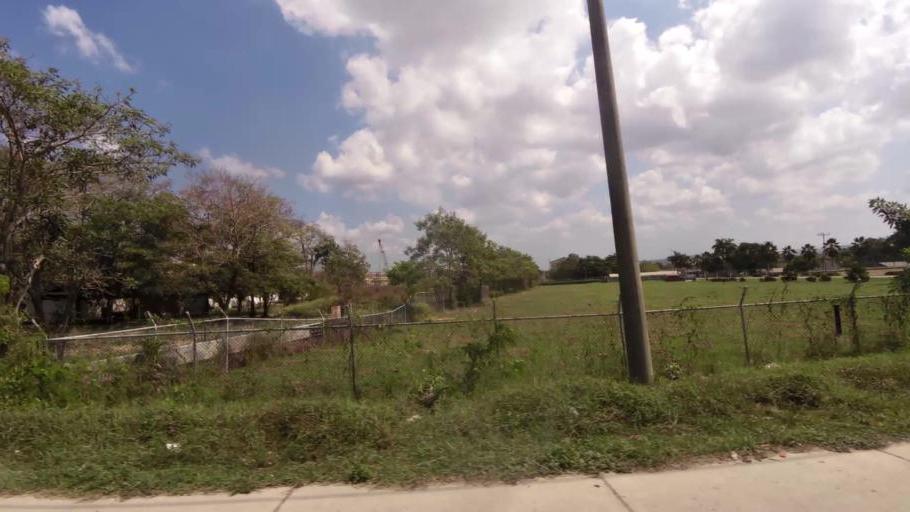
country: CO
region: Bolivar
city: Cartagena
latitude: 10.3484
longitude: -75.4949
